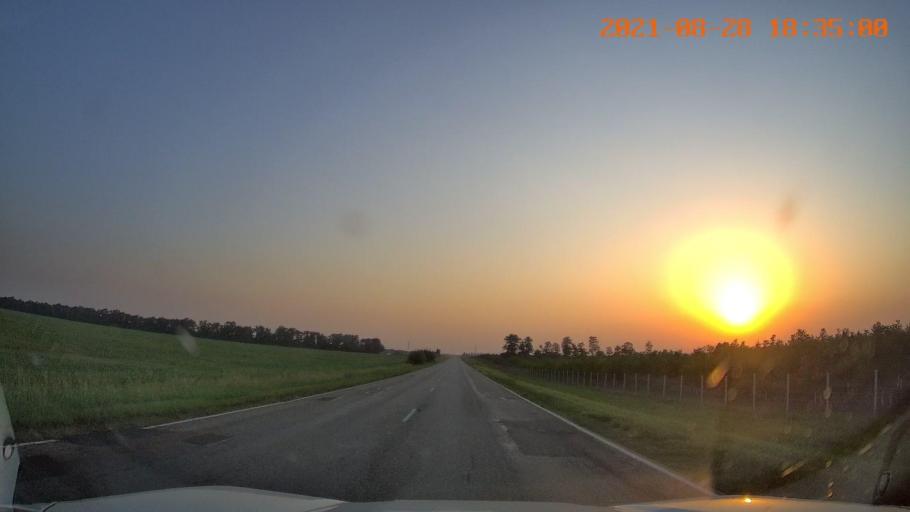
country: RU
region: Adygeya
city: Giaginskaya
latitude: 44.8756
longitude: 40.1429
